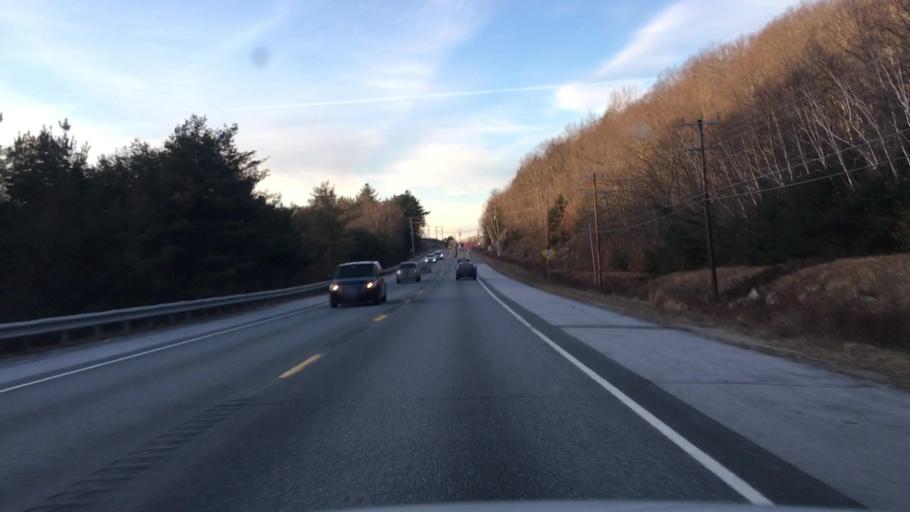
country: US
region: Maine
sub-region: Hancock County
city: Dedham
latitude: 44.7235
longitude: -68.6184
